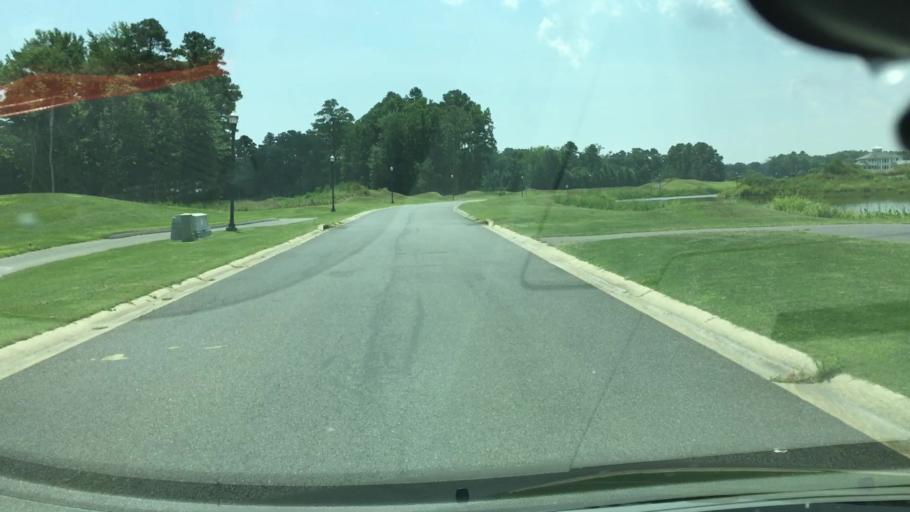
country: US
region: Maryland
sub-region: Worcester County
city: Ocean Pines
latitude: 38.3478
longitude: -75.1522
